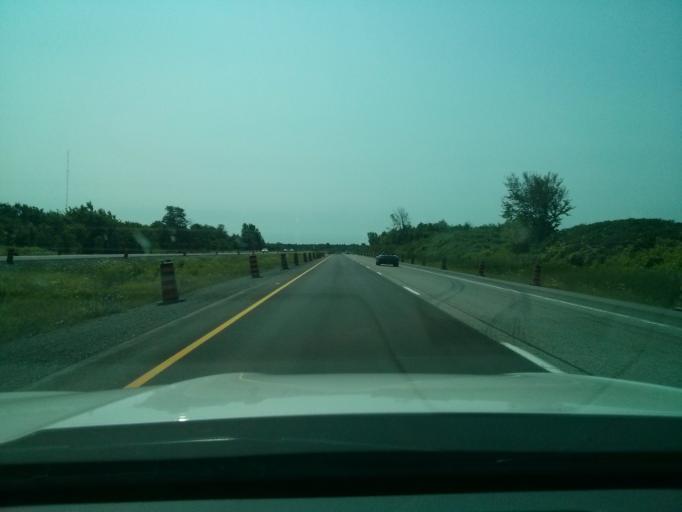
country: CA
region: Ontario
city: Bells Corners
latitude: 45.2587
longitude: -75.7873
